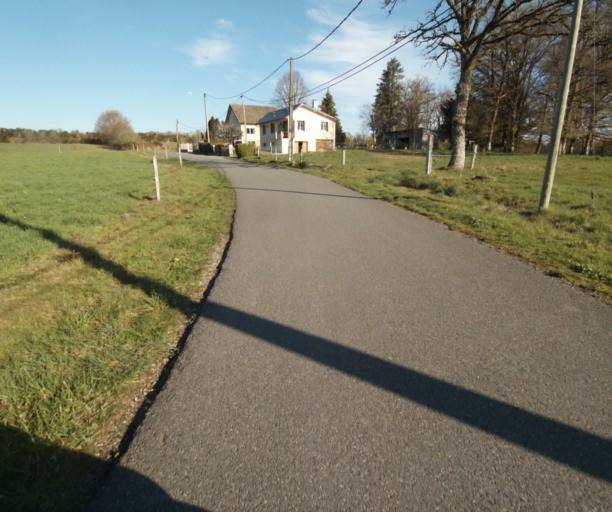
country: FR
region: Limousin
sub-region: Departement de la Correze
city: Correze
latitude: 45.3199
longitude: 1.8882
